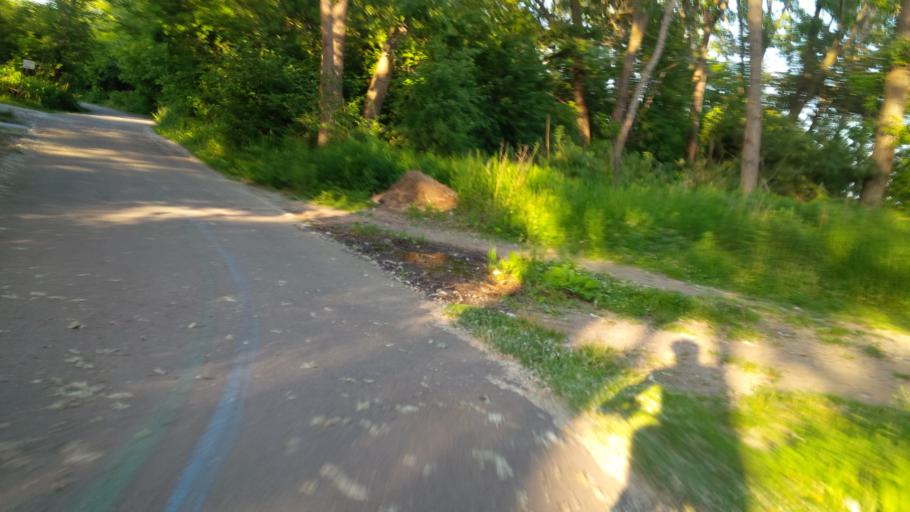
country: CA
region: Ontario
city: Toronto
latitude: 43.6394
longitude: -79.3415
